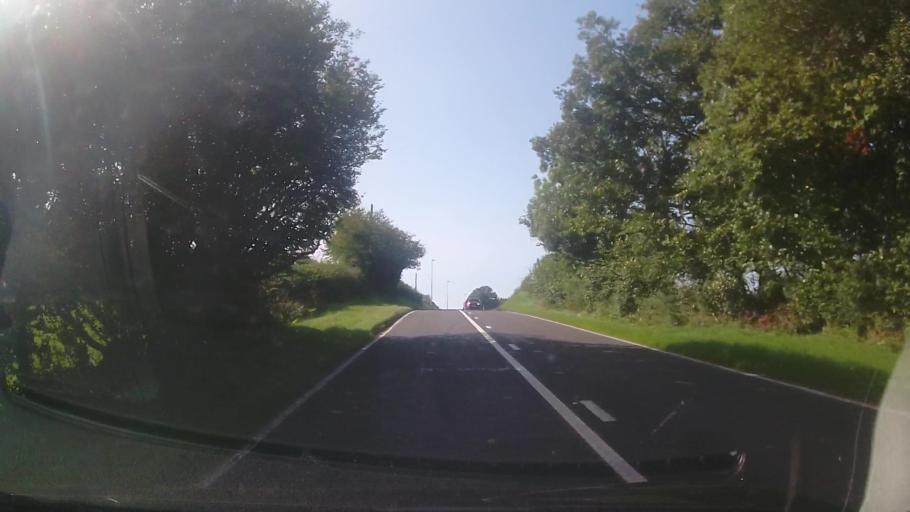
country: GB
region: Wales
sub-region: Sir Powys
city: Builth Wells
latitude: 52.1364
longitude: -3.5252
